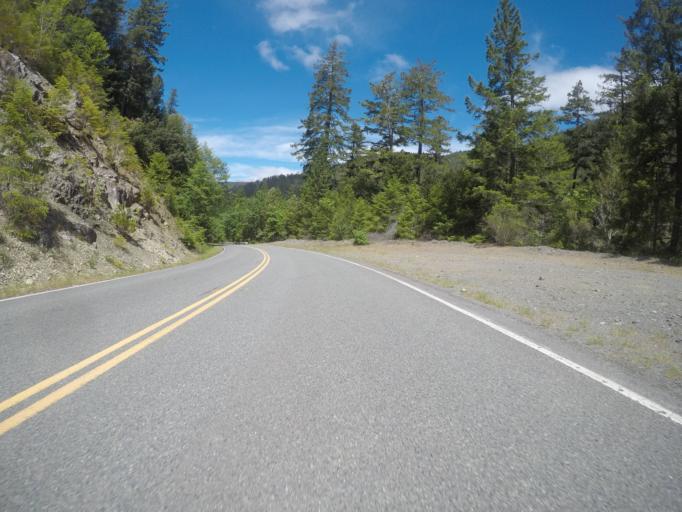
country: US
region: California
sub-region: Del Norte County
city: Bertsch-Oceanview
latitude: 41.7260
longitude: -123.9571
